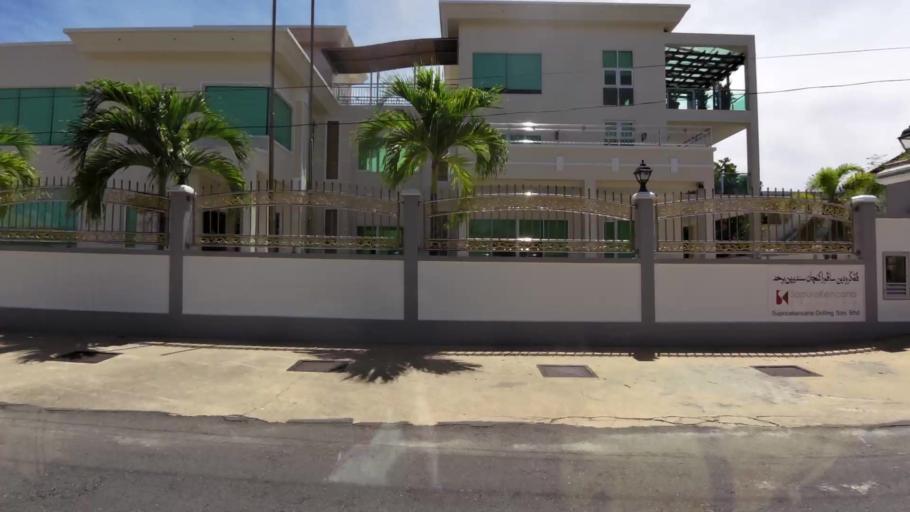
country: BN
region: Belait
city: Kuala Belait
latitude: 4.5908
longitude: 114.2222
